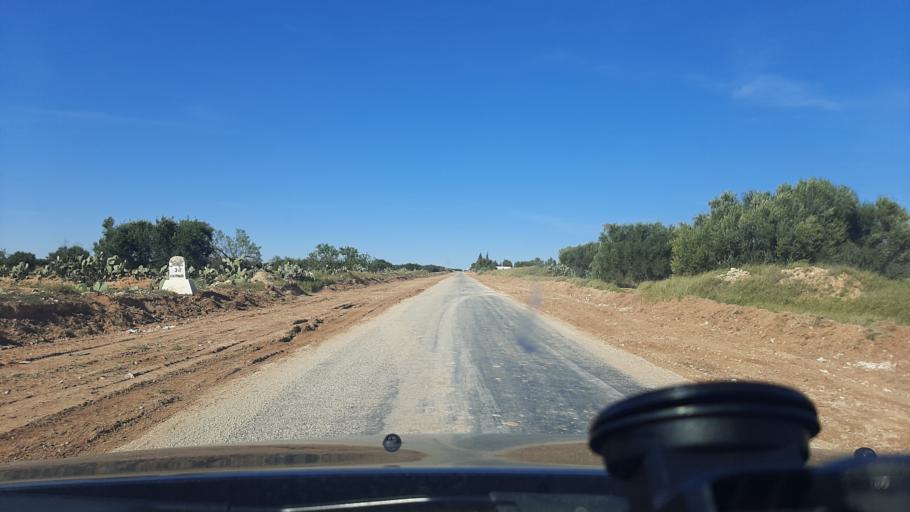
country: TN
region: Safaqis
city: Sfax
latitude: 34.9385
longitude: 10.5602
